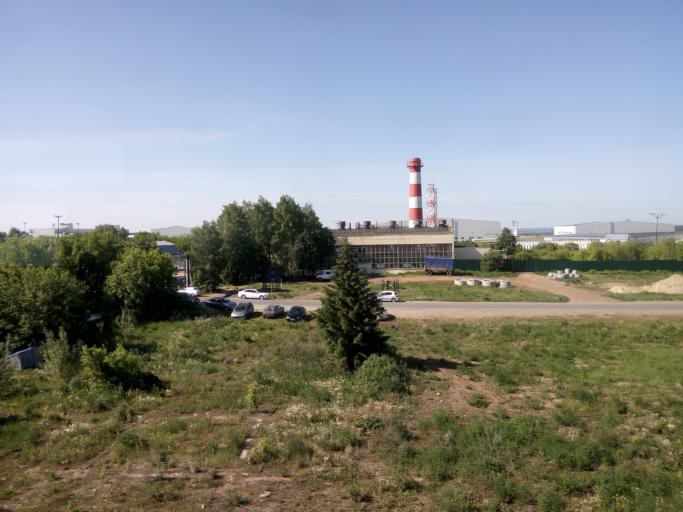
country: RU
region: Tatarstan
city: Stolbishchi
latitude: 55.6159
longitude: 49.2823
